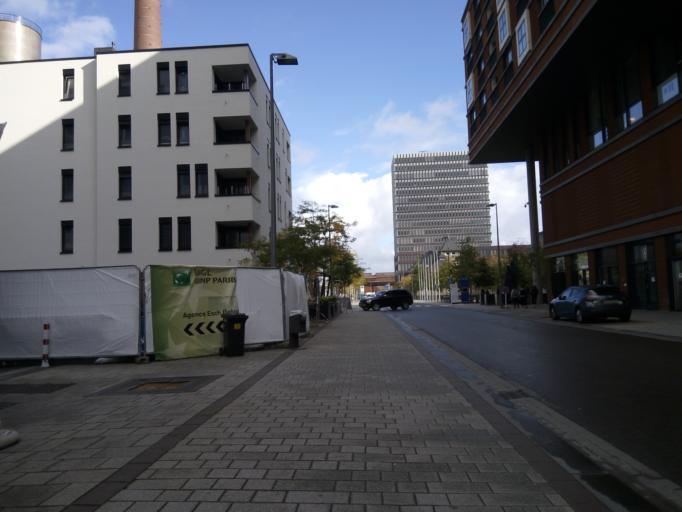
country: FR
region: Lorraine
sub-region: Departement de la Moselle
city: Russange
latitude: 49.5009
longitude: 5.9463
